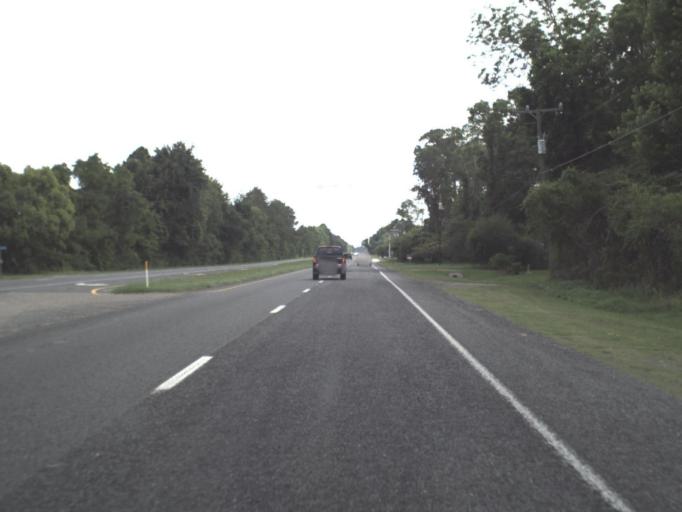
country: US
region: Florida
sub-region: Nassau County
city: Nassau Village-Ratliff
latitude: 30.5227
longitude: -81.8002
